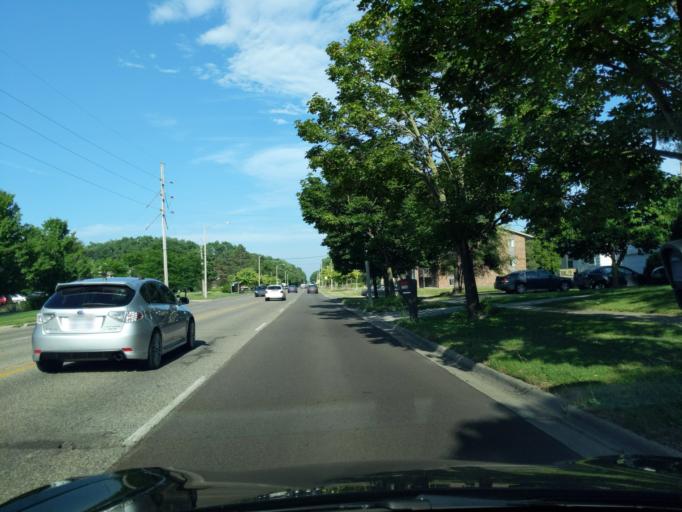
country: US
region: Michigan
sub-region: Ingham County
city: East Lansing
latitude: 42.7469
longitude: -84.4570
